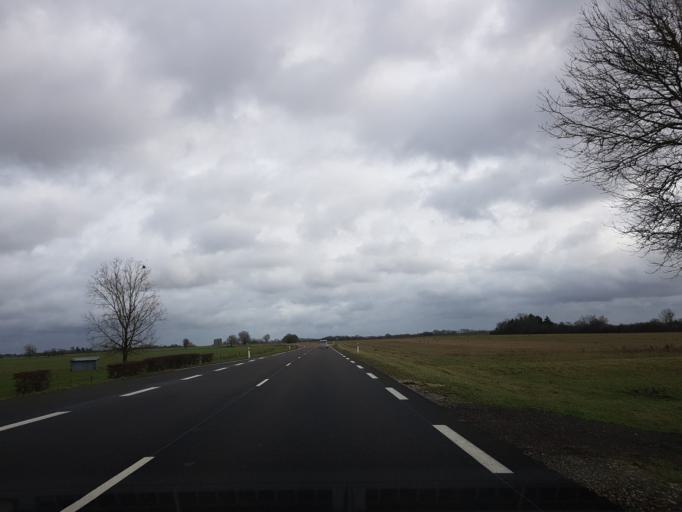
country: FR
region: Champagne-Ardenne
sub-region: Departement de la Haute-Marne
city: Chalindrey
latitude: 47.8473
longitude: 5.4303
